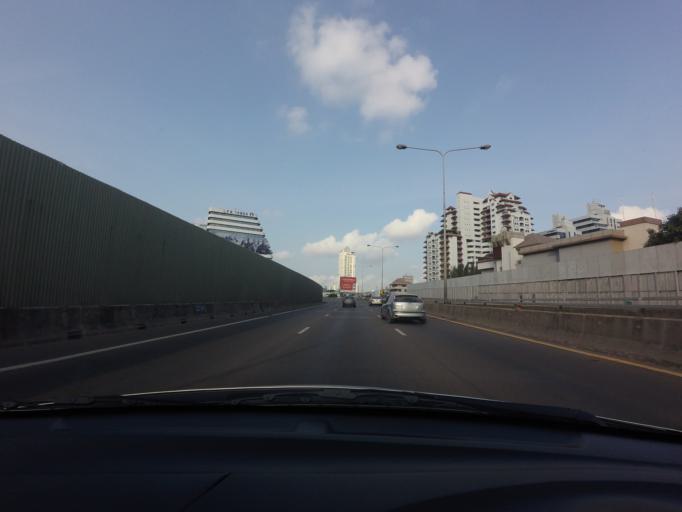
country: TH
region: Bangkok
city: Yan Nawa
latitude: 13.7051
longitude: 100.5455
